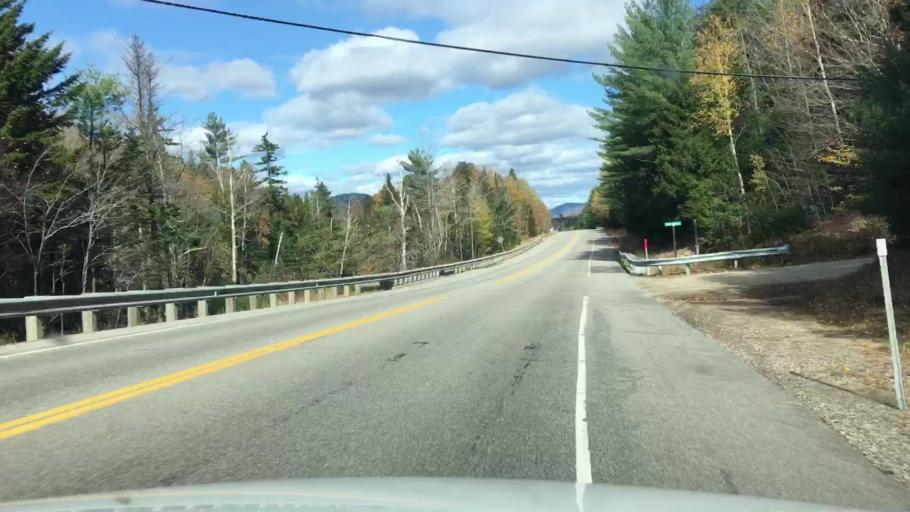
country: US
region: New Hampshire
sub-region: Coos County
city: Gorham
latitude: 44.3081
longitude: -71.2204
